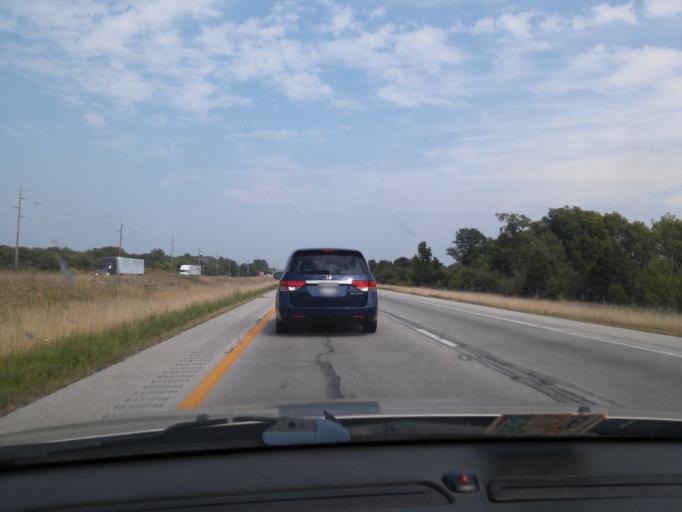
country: US
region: Ohio
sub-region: Preble County
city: Lewisburg
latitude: 39.8359
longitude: -84.5885
